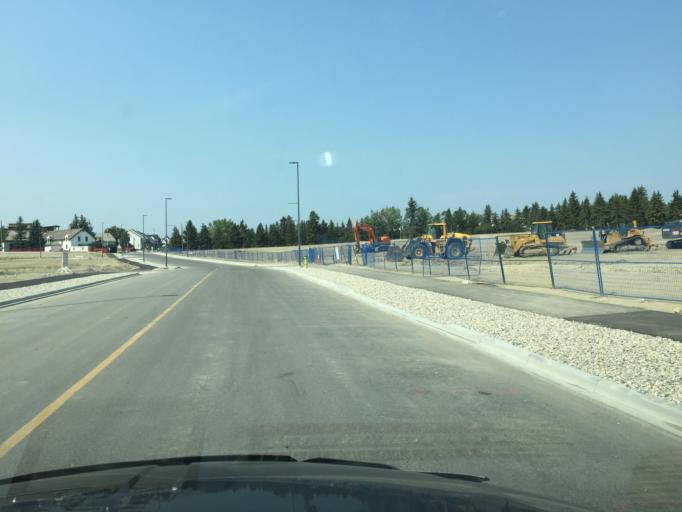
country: CA
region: Alberta
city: Calgary
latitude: 51.0180
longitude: -114.1241
